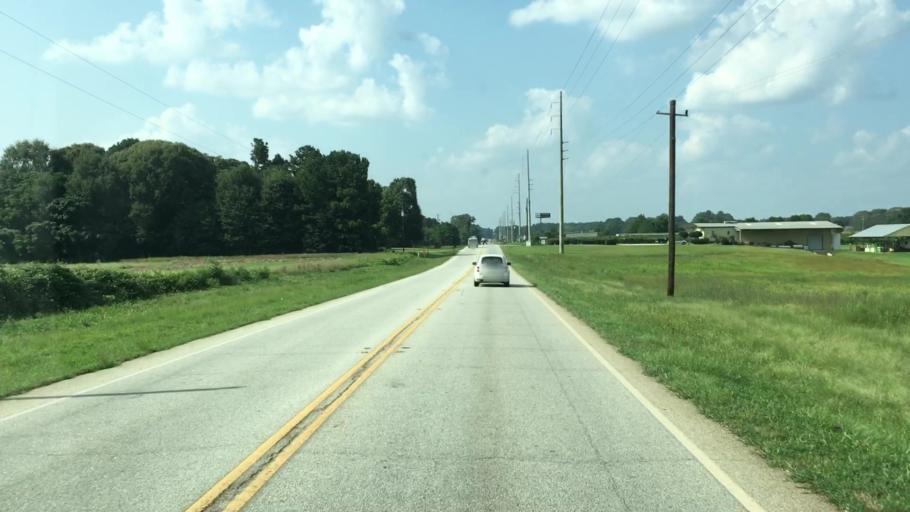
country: US
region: Georgia
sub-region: Walton County
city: Social Circle
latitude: 33.5915
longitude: -83.7484
